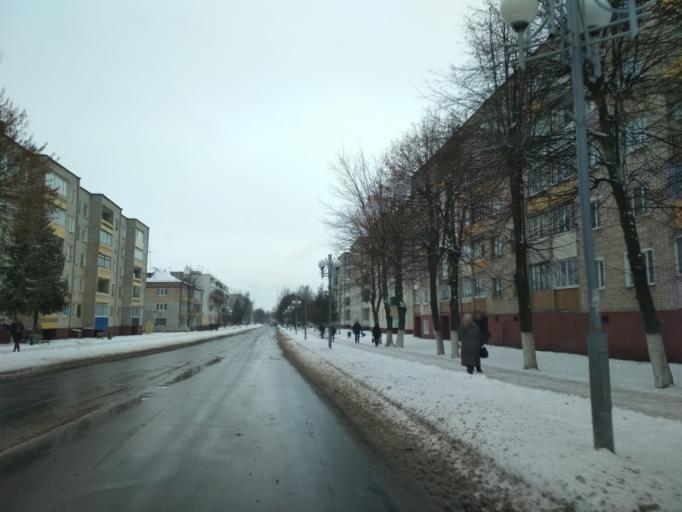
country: BY
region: Minsk
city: Mar''ina Horka
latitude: 53.5130
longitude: 28.1466
